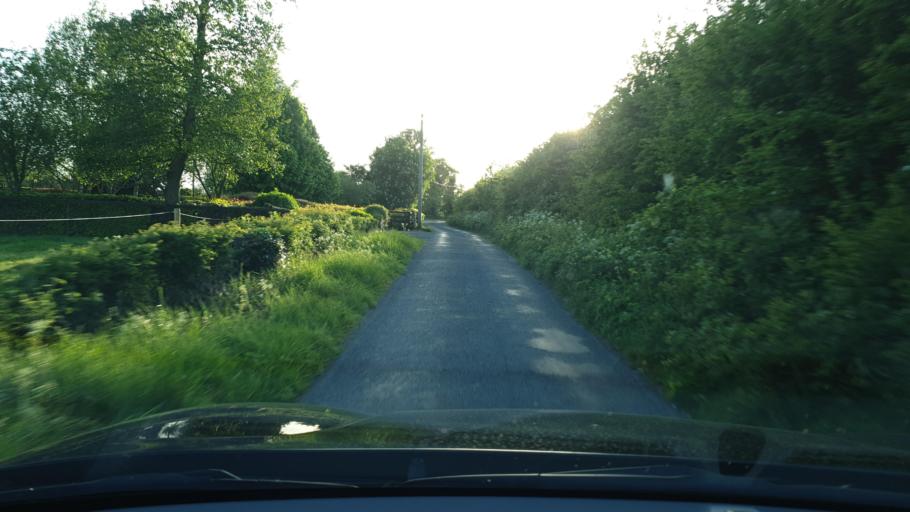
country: IE
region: Leinster
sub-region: An Mhi
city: Ashbourne
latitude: 53.4786
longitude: -6.3782
